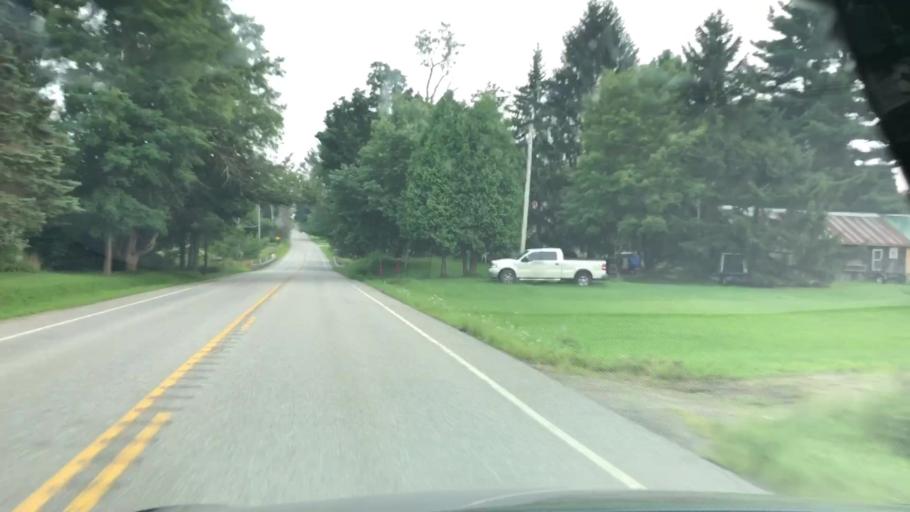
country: US
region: Pennsylvania
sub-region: Erie County
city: Union City
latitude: 41.9245
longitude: -79.8435
